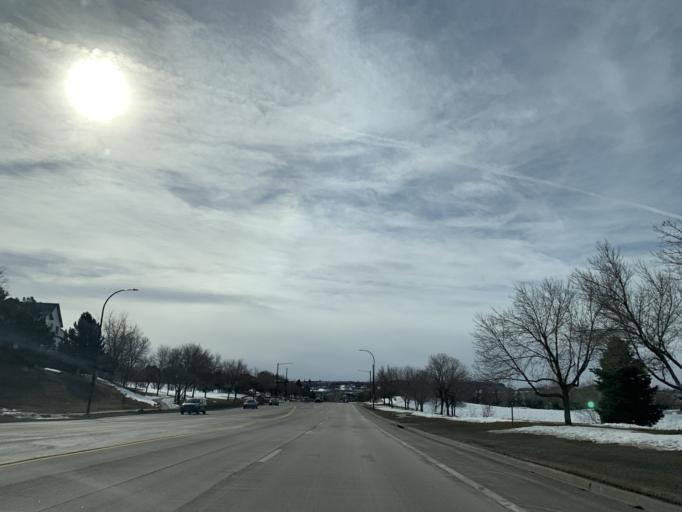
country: US
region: Colorado
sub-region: Douglas County
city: Carriage Club
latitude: 39.5274
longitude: -104.9169
